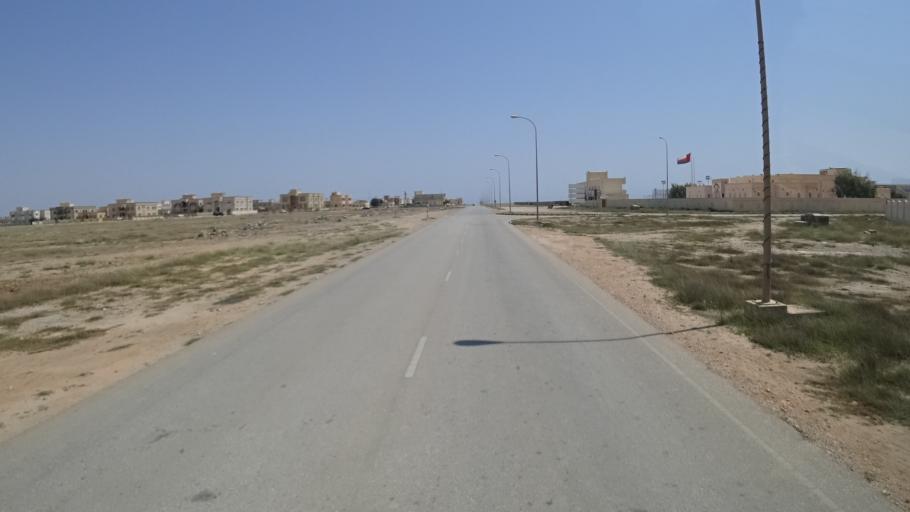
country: OM
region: Zufar
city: Salalah
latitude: 16.9849
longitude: 54.7007
